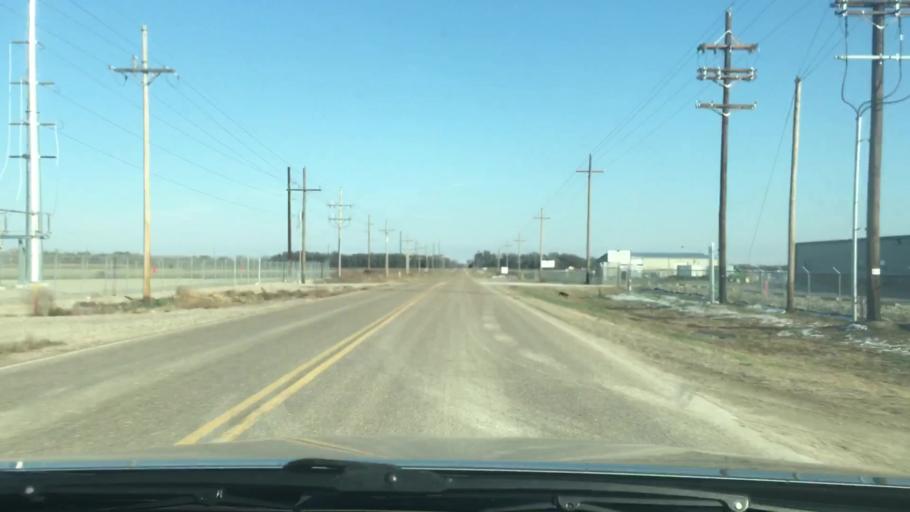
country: US
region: Kansas
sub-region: Rice County
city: Lyons
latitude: 38.2896
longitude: -98.1926
